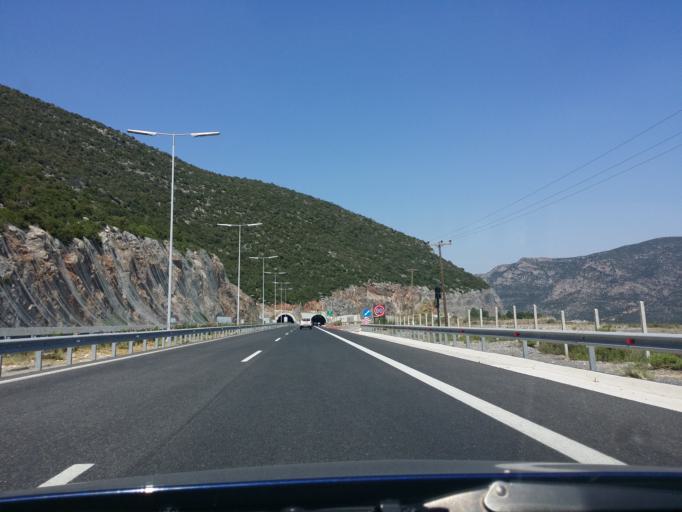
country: GR
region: Peloponnese
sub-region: Nomos Korinthias
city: Nemea
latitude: 37.6866
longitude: 22.5154
